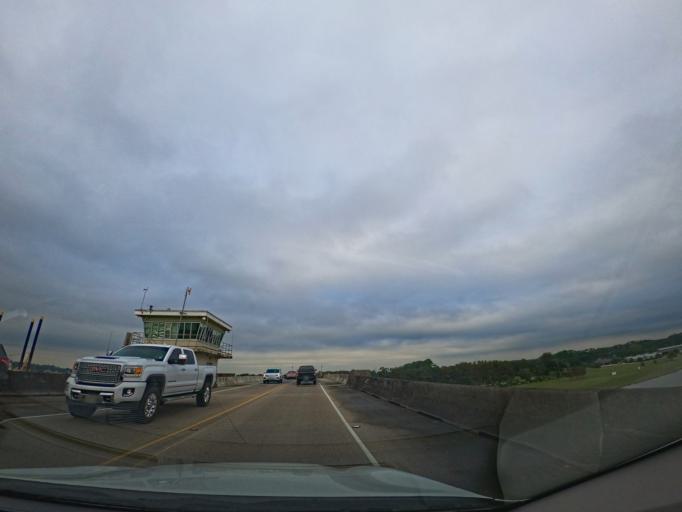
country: US
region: Louisiana
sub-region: Terrebonne Parish
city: Houma
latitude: 29.5680
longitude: -90.7206
